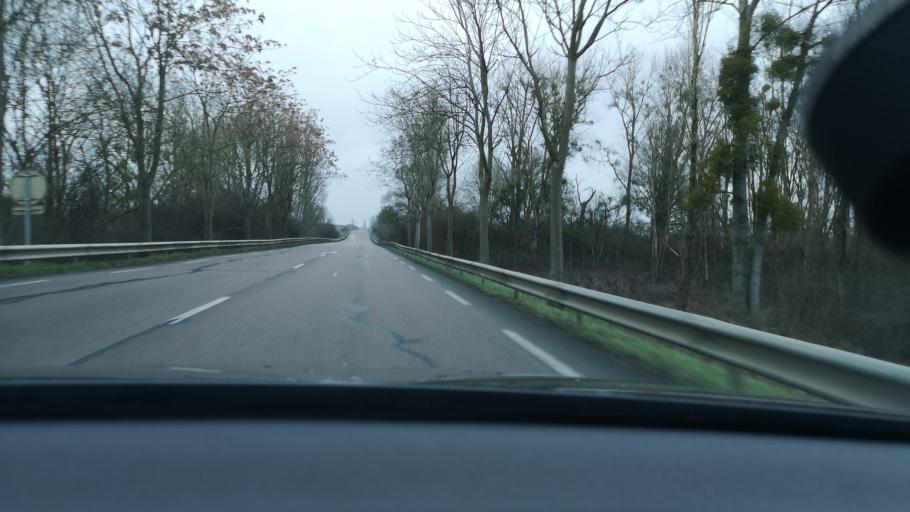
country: FR
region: Bourgogne
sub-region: Departement de la Cote-d'Or
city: Seurre
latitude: 46.9424
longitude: 5.1522
